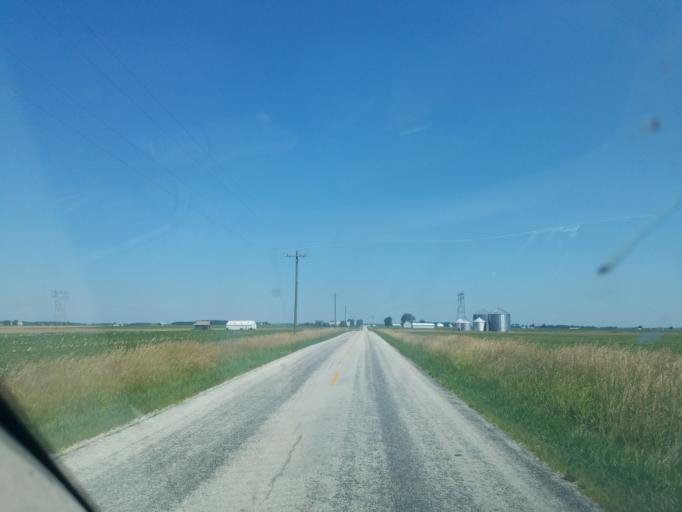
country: US
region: Ohio
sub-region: Mercer County
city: Rockford
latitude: 40.6132
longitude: -84.7085
